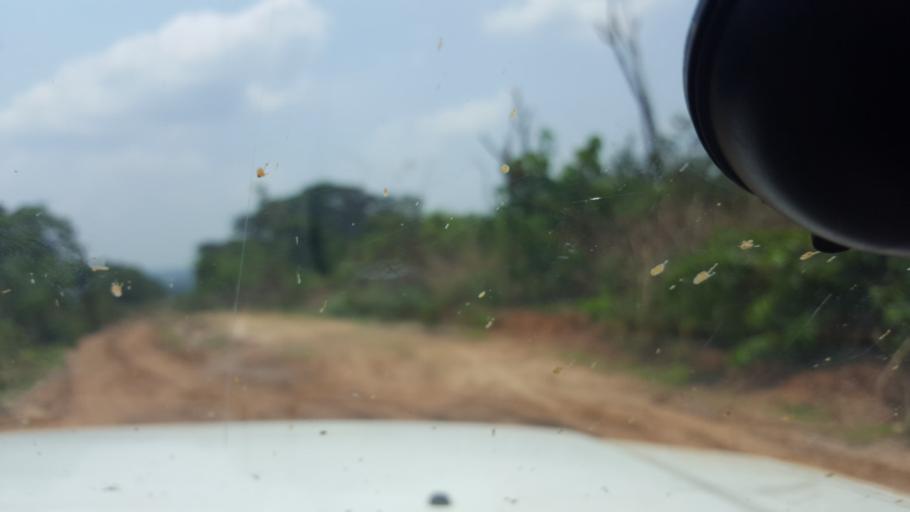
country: CD
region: Bandundu
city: Mushie
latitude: -3.7512
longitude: 16.6371
